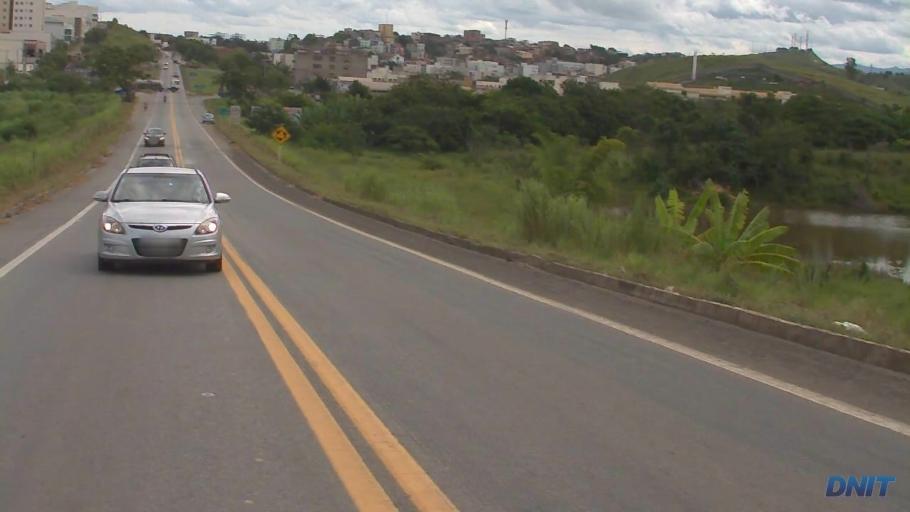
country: BR
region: Minas Gerais
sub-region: Ipatinga
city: Ipatinga
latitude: -19.4526
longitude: -42.5198
